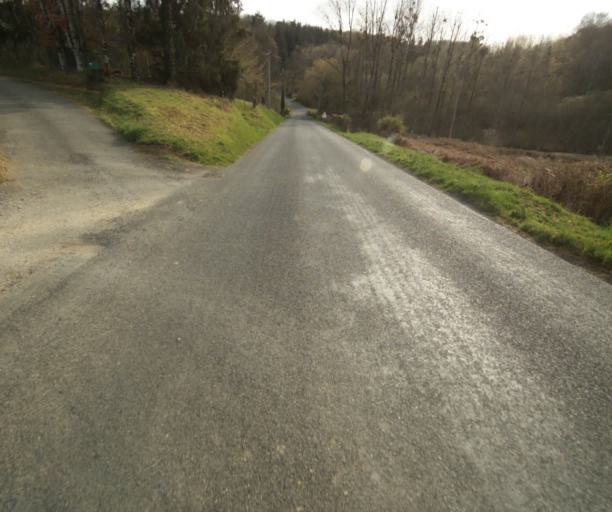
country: FR
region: Limousin
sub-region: Departement de la Correze
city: Naves
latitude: 45.3149
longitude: 1.7576
